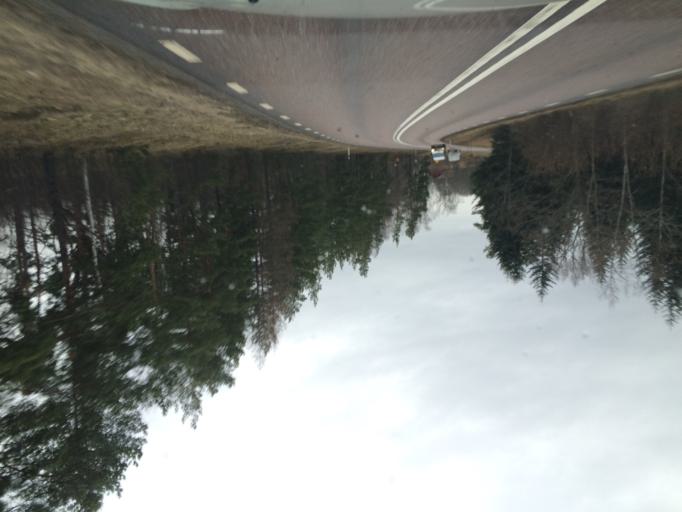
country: SE
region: Soedermanland
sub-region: Katrineholms Kommun
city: Katrineholm
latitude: 59.1465
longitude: 16.1178
